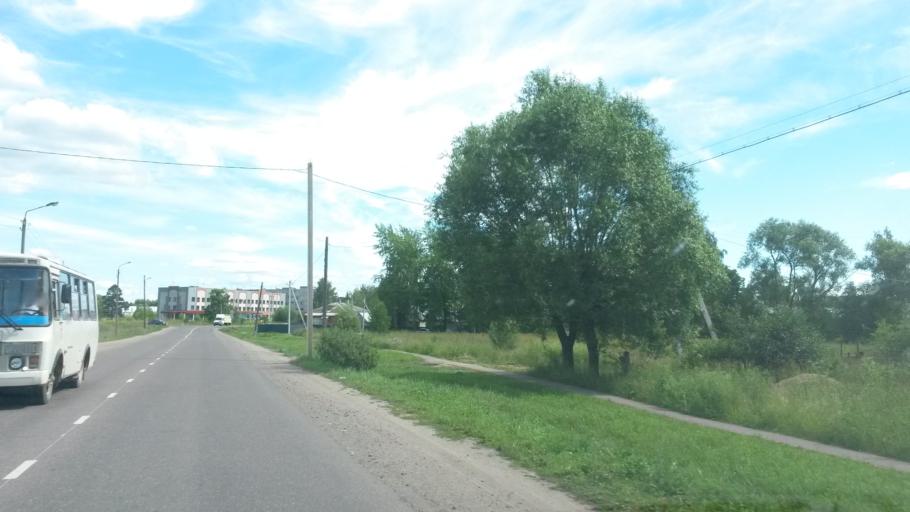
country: RU
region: Ivanovo
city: Zavolzhsk
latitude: 57.4975
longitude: 42.1294
